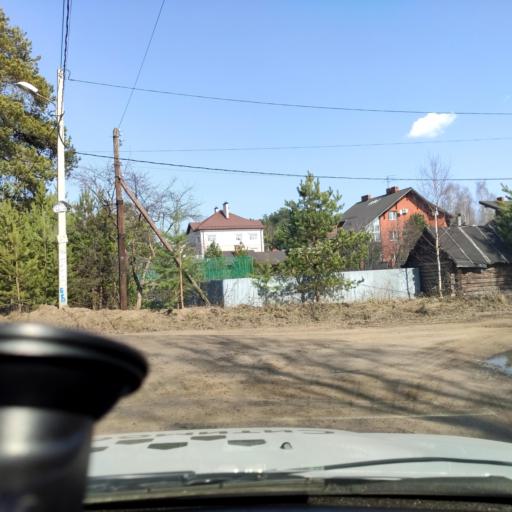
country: RU
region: Perm
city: Perm
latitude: 58.0550
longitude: 56.2888
